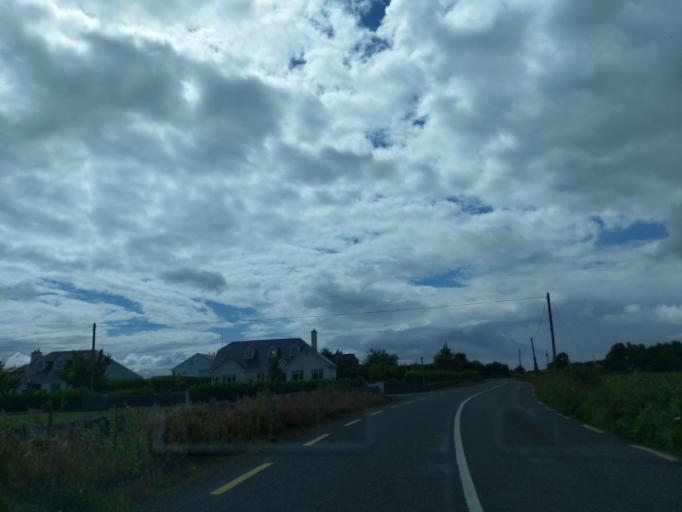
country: IE
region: Connaught
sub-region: County Galway
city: Athenry
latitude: 53.2814
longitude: -8.8312
